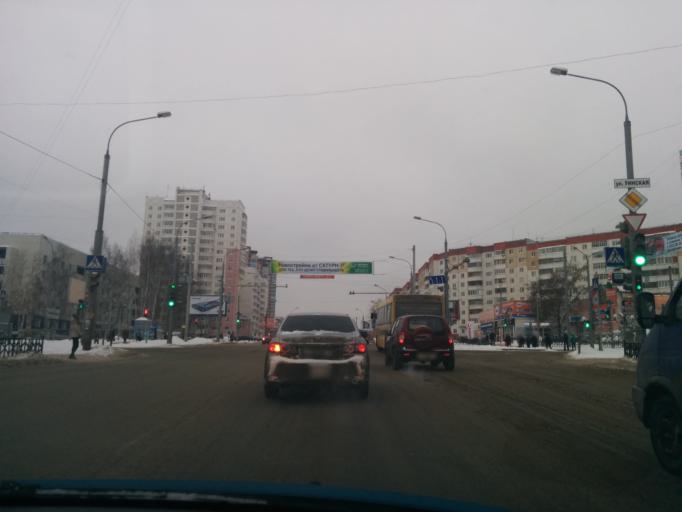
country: RU
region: Perm
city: Perm
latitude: 58.0060
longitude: 56.3076
